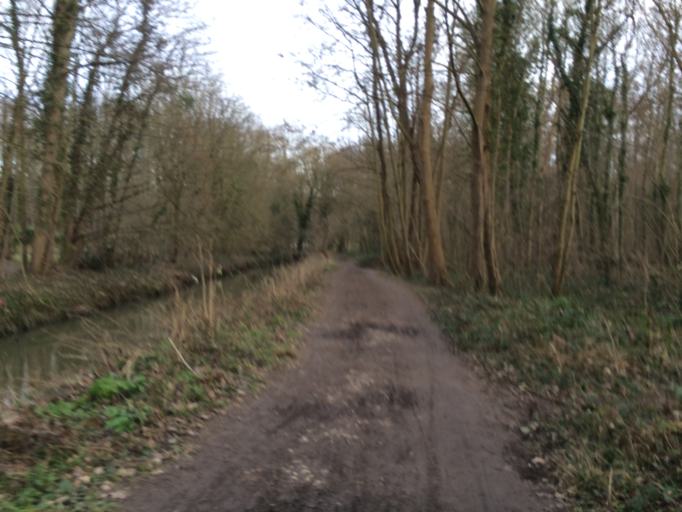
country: FR
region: Ile-de-France
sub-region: Departement de l'Essonne
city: Epinay-sur-Orge
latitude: 48.6819
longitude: 2.3241
